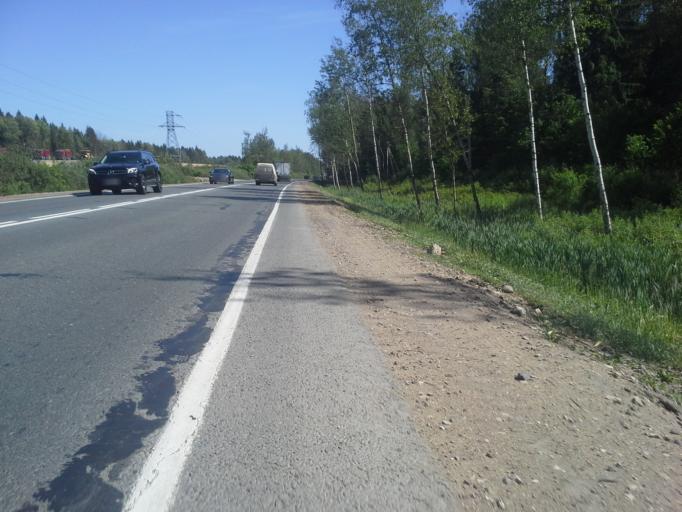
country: RU
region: Moskovskaya
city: Aprelevka
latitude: 55.4437
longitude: 37.1398
